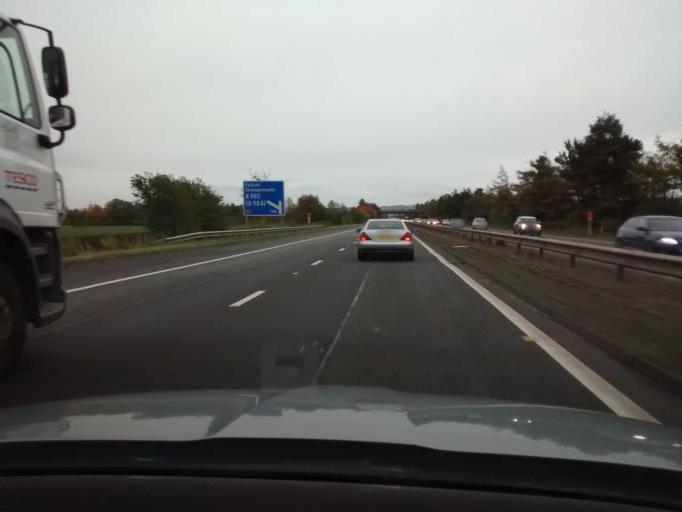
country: GB
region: Scotland
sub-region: Falkirk
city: Airth
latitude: 56.0329
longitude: -3.7660
